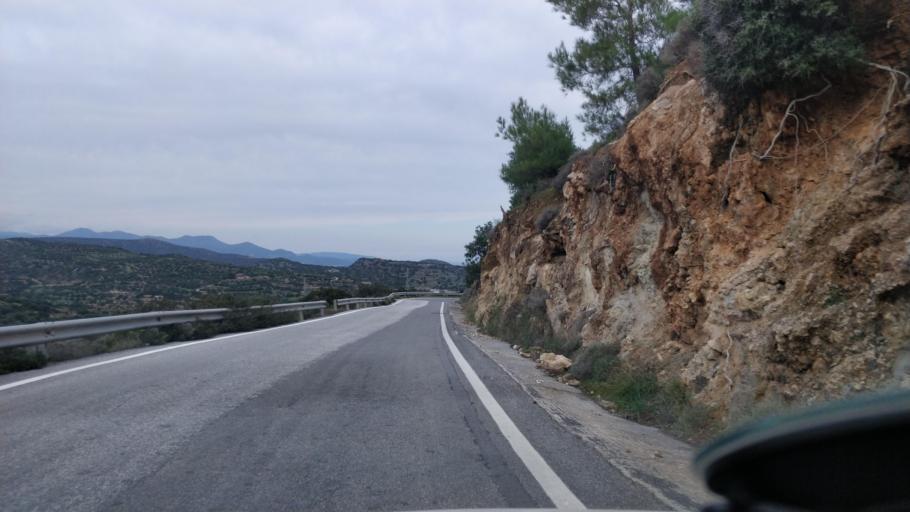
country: GR
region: Crete
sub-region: Nomos Lasithiou
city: Agios Nikolaos
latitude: 35.1066
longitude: 25.7119
